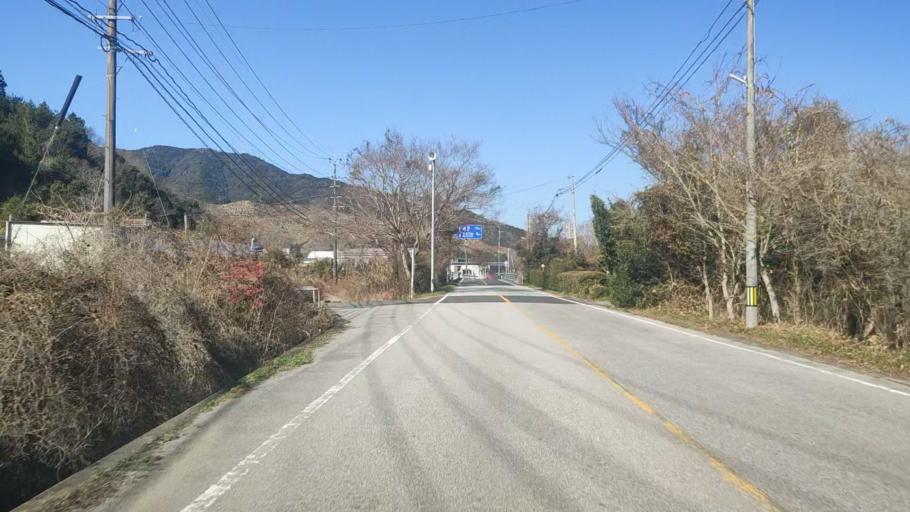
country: JP
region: Oita
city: Saiki
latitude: 32.9067
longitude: 131.9315
